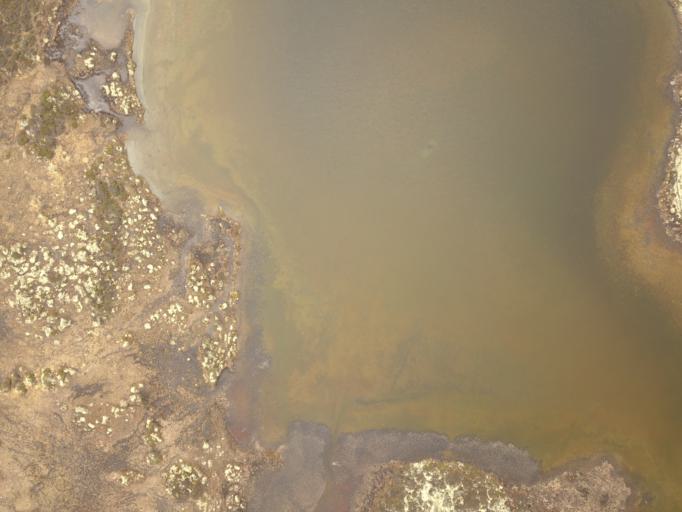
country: NO
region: Hedmark
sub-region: Folldal
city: Folldal
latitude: 62.2283
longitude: 9.6445
